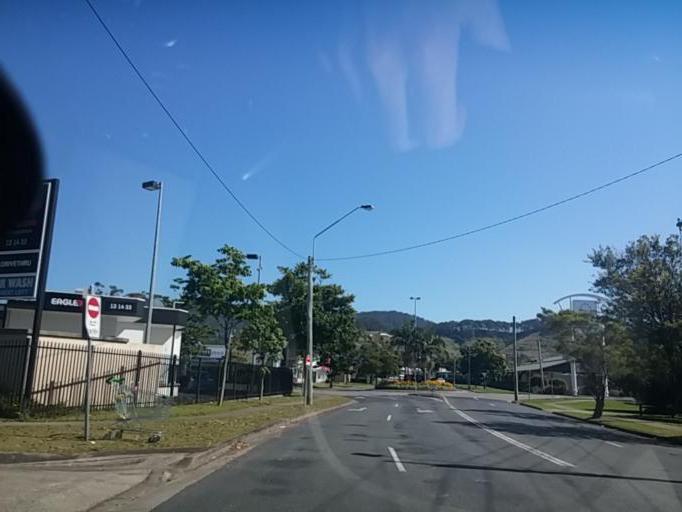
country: AU
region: New South Wales
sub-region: Coffs Harbour
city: Coffs Harbour
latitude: -30.2847
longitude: 153.1297
